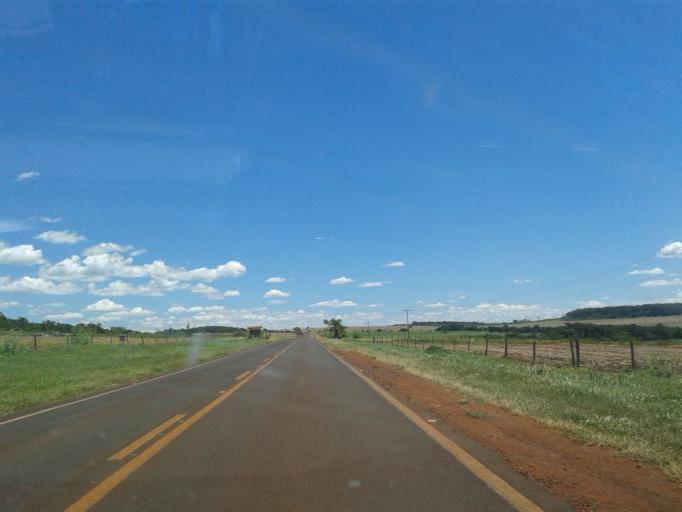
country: BR
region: Minas Gerais
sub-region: Capinopolis
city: Capinopolis
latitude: -18.6191
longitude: -49.5327
